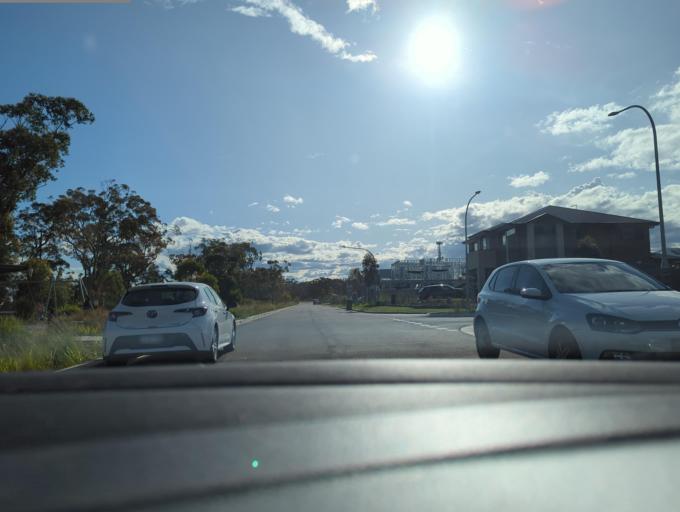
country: AU
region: New South Wales
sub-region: Sutherland Shire
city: Woronora Heights
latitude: -34.0391
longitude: 151.0032
